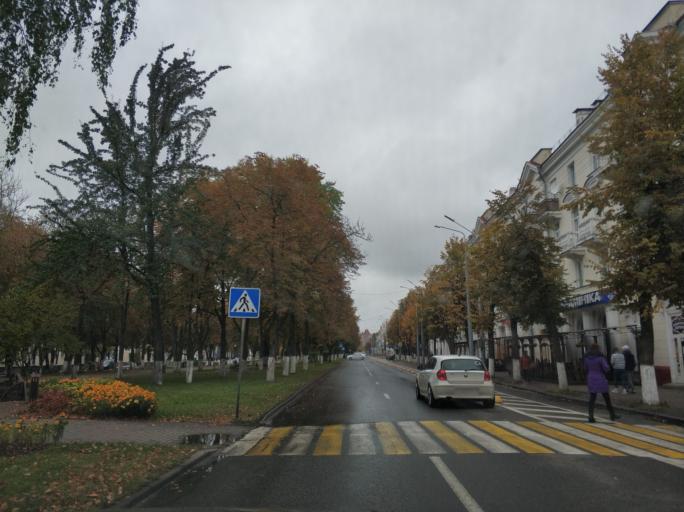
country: BY
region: Vitebsk
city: Polatsk
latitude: 55.4848
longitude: 28.7764
